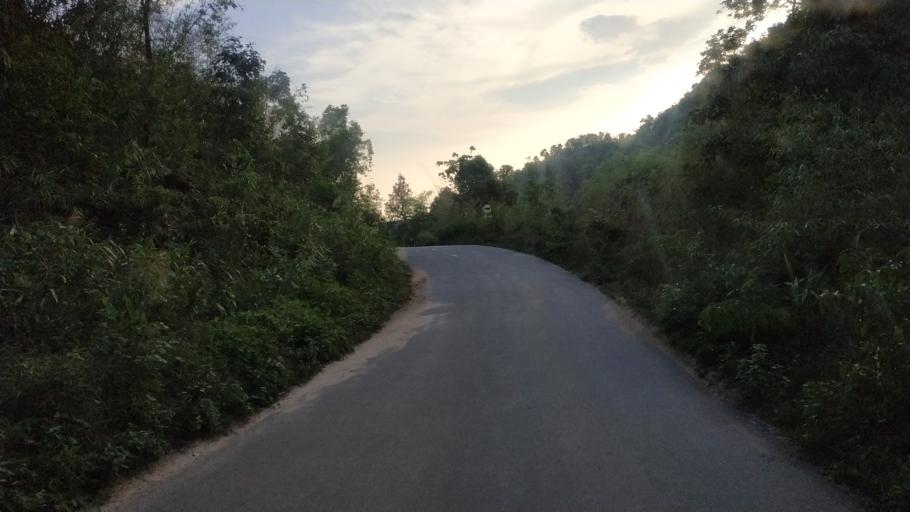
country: MM
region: Mon
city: Kyaikto
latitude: 17.4233
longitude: 97.0756
